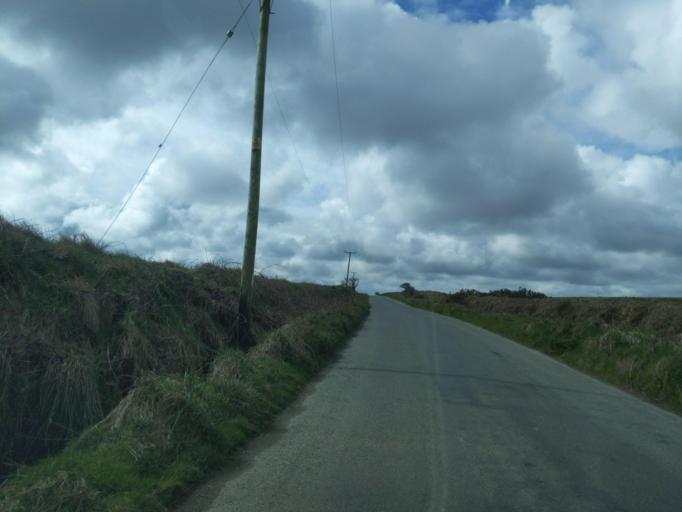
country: GB
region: England
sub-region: Cornwall
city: Camelford
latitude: 50.6409
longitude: -4.6390
